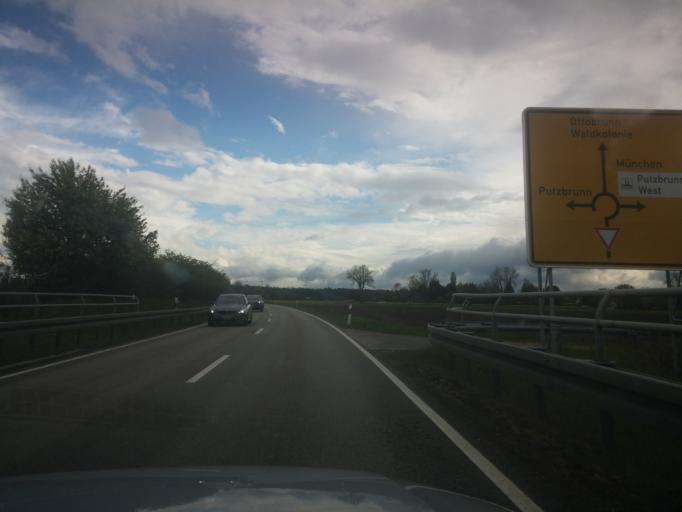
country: DE
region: Bavaria
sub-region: Upper Bavaria
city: Putzbrunn
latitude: 48.0808
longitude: 11.7093
